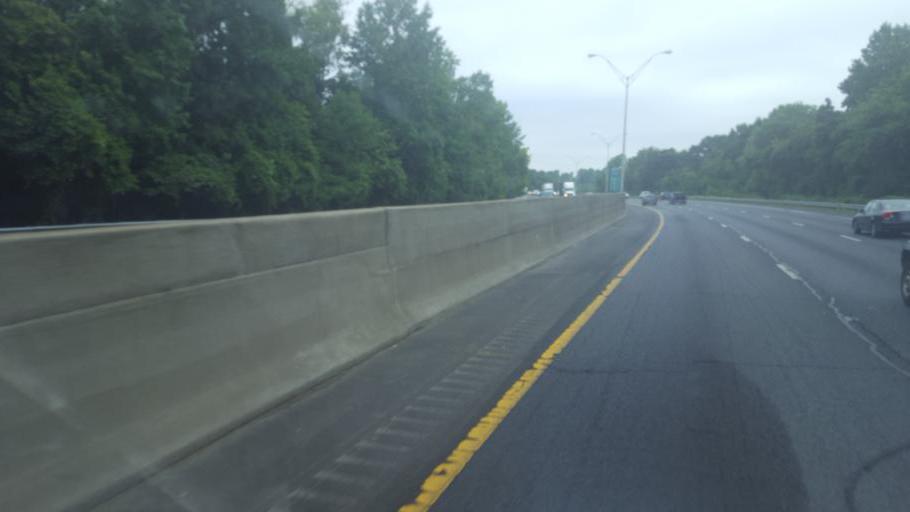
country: US
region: North Carolina
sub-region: Mecklenburg County
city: Charlotte
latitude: 35.2147
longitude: -80.8727
